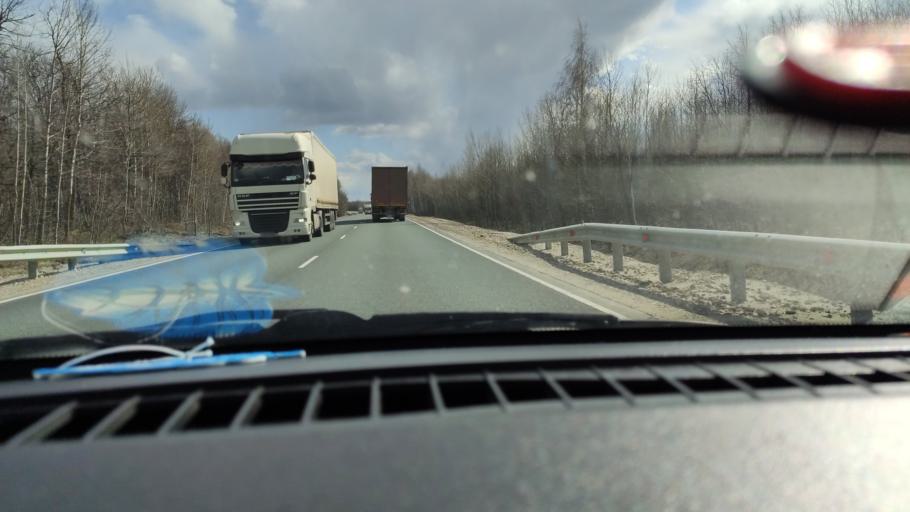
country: RU
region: Saratov
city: Khvalynsk
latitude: 52.4797
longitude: 48.0131
